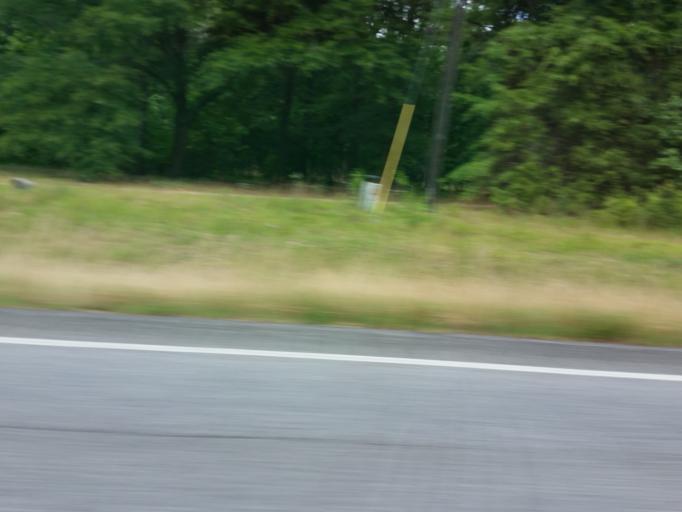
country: US
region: Alabama
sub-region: Sumter County
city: York
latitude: 32.3958
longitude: -88.2085
